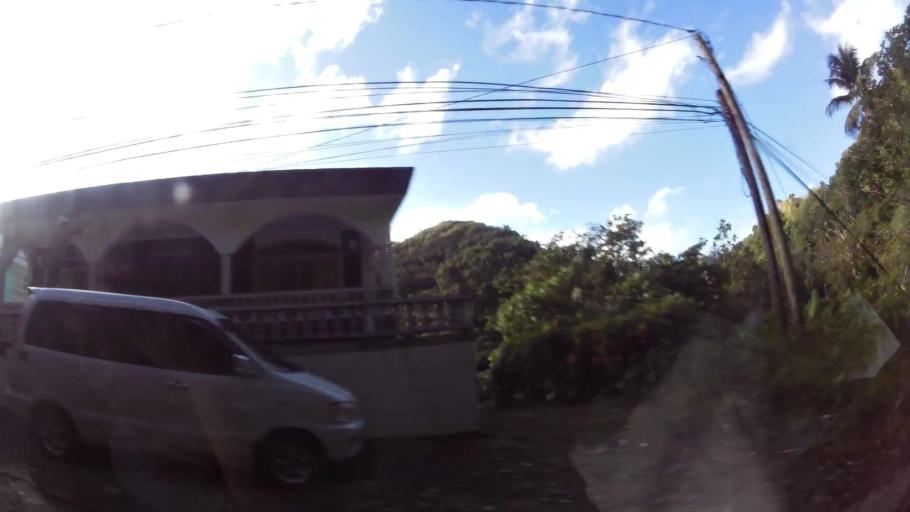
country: DM
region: Saint Andrew
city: Calibishie
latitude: 15.5865
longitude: -61.4076
